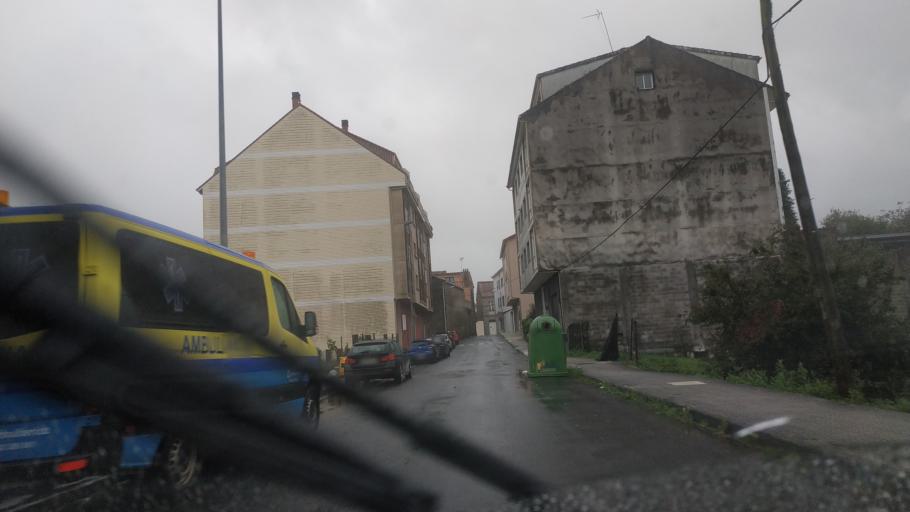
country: ES
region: Galicia
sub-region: Provincia da Coruna
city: Negreira
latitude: 42.9093
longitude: -8.7384
